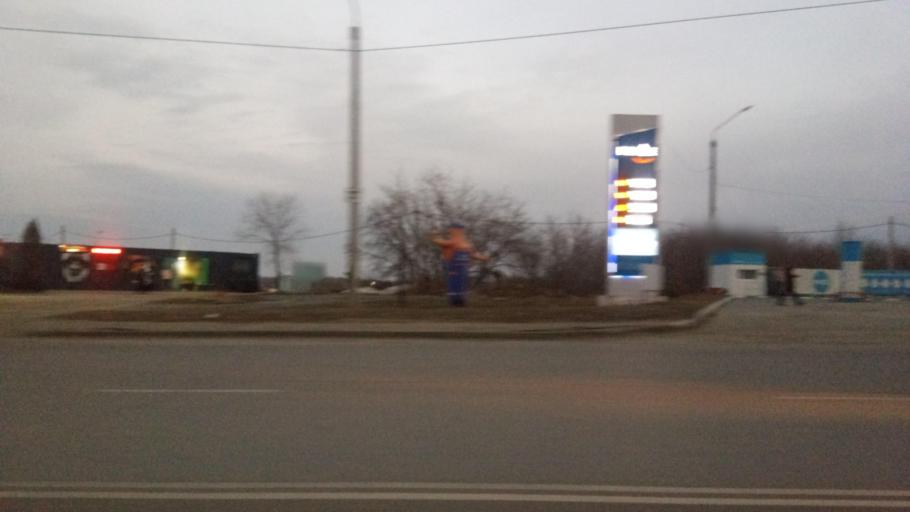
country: RU
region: Chelyabinsk
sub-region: Gorod Chelyabinsk
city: Chelyabinsk
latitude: 55.1727
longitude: 61.4867
